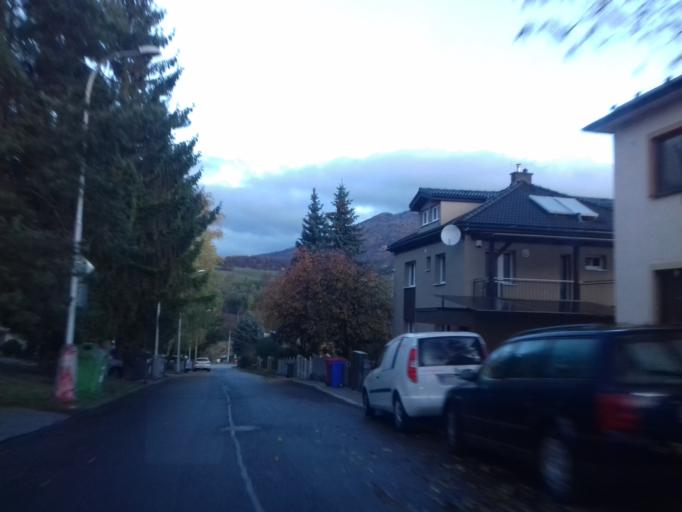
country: SK
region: Banskobystricky
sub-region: Okres Banska Bystrica
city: Banska Bystrica
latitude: 48.7549
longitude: 19.1544
